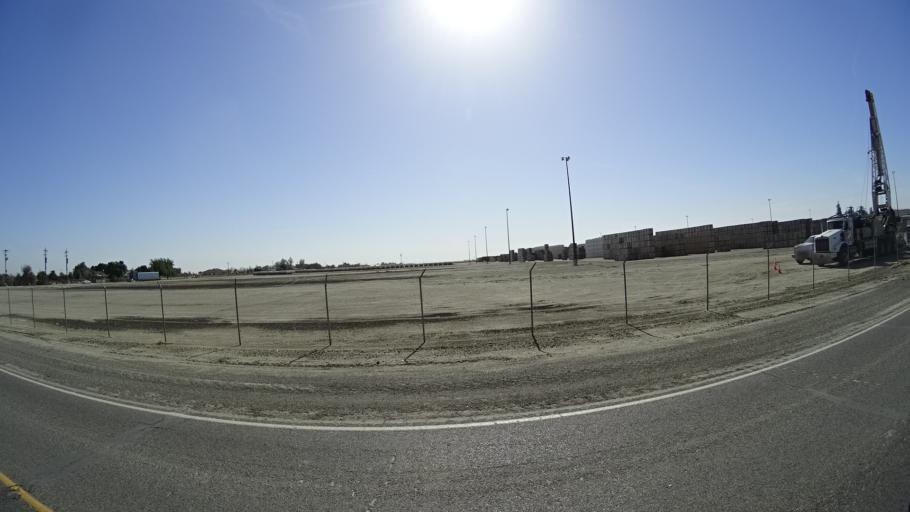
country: US
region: California
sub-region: Kings County
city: Corcoran
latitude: 36.0713
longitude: -119.5720
